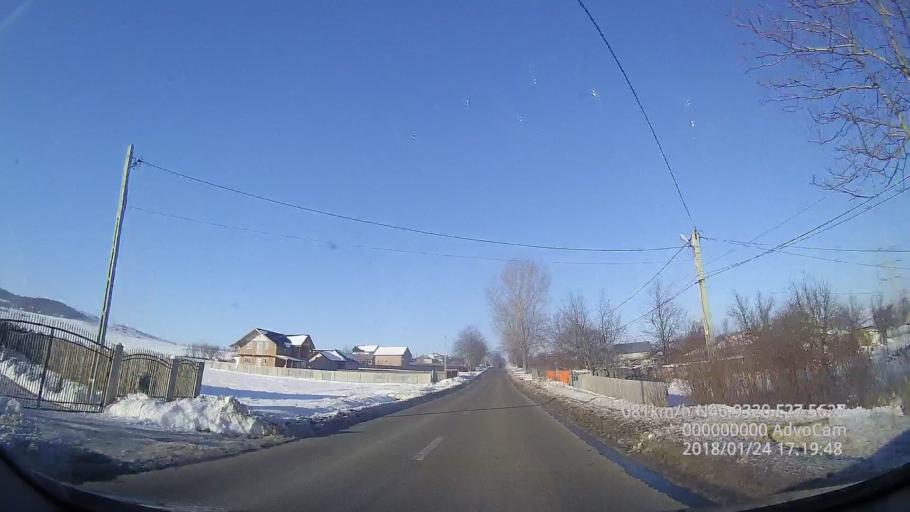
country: RO
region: Iasi
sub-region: Comuna Scanteia
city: Scanteia
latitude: 46.9327
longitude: 27.5626
